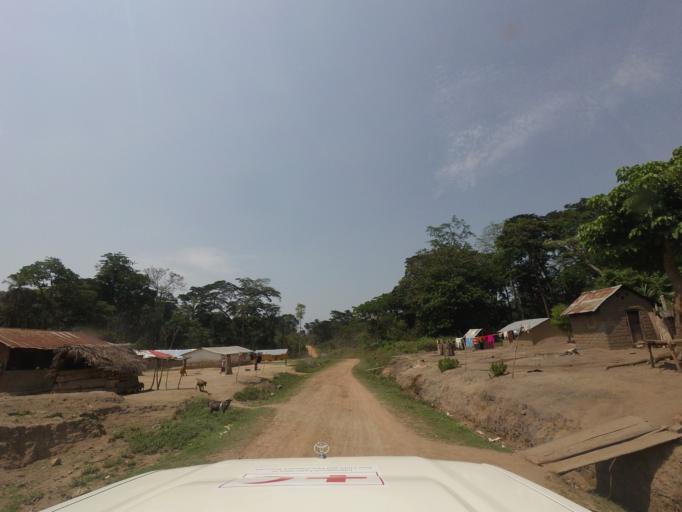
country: LR
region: Lofa
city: Voinjama
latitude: 8.4870
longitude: -9.6624
